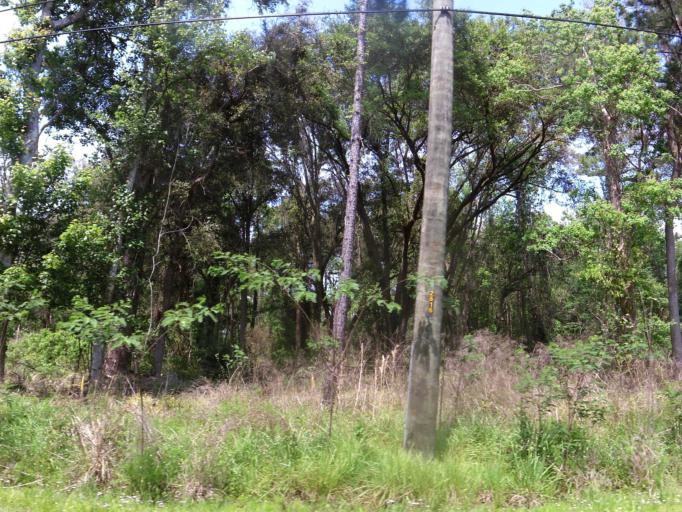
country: US
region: Florida
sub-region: Nassau County
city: Nassau Village-Ratliff
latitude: 30.5223
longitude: -81.6797
